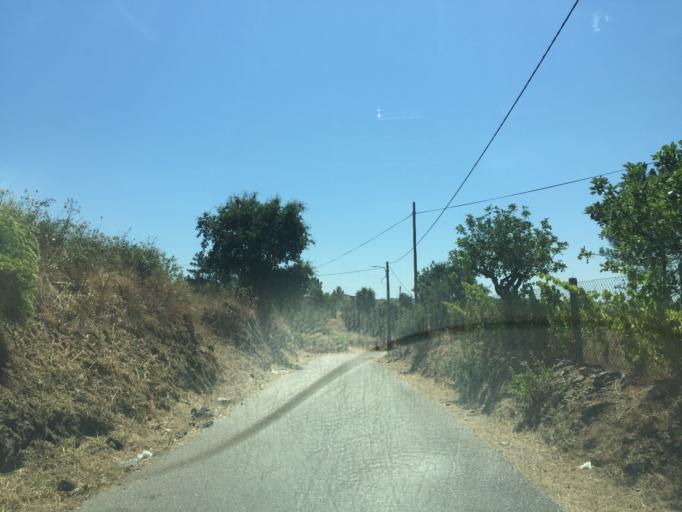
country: PT
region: Santarem
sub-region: Tomar
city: Tomar
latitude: 39.5750
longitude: -8.2990
